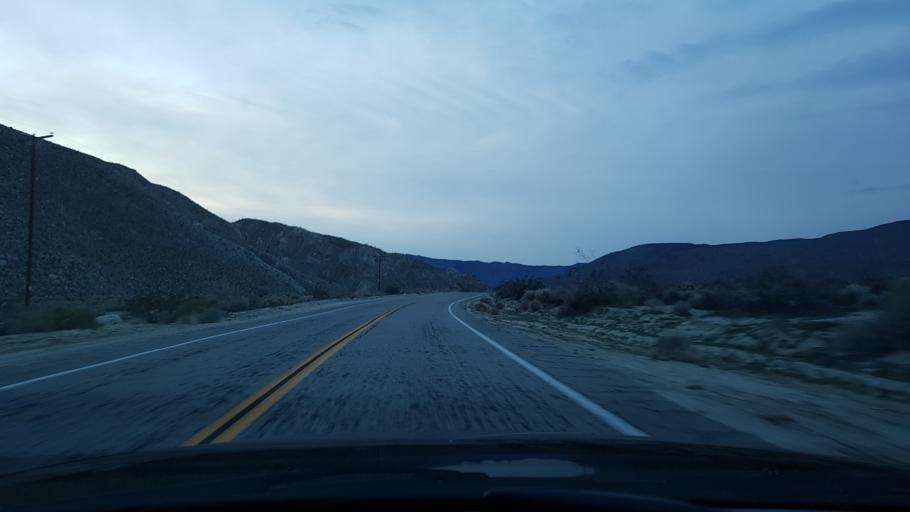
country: US
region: California
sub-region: San Diego County
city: Pine Valley
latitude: 32.9695
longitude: -116.3339
